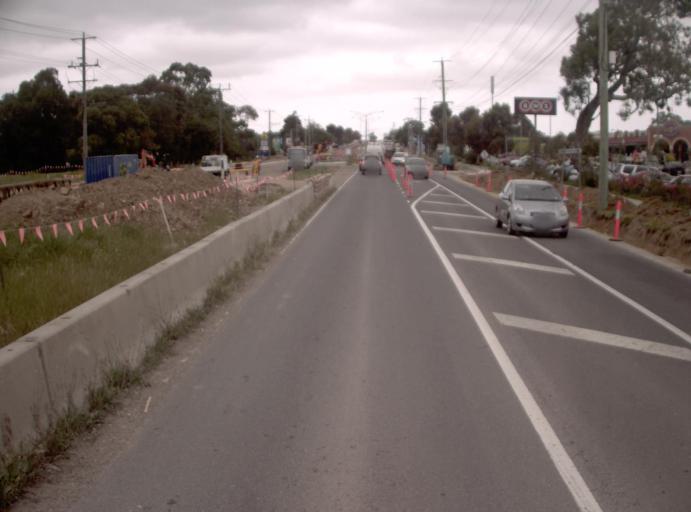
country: AU
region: Victoria
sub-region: Casey
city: Hallam
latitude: -38.0324
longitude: 145.2679
